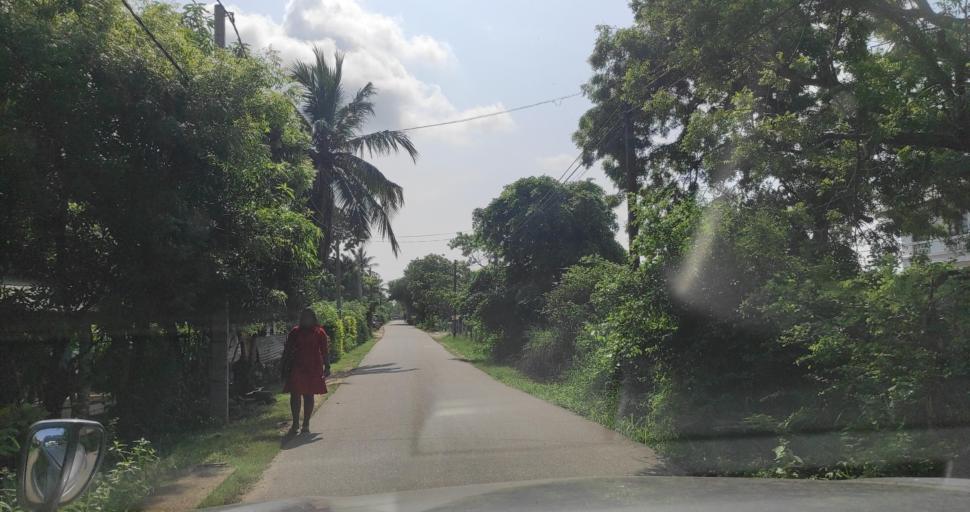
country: LK
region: Eastern Province
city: Trincomalee
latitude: 8.3799
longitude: 81.0110
